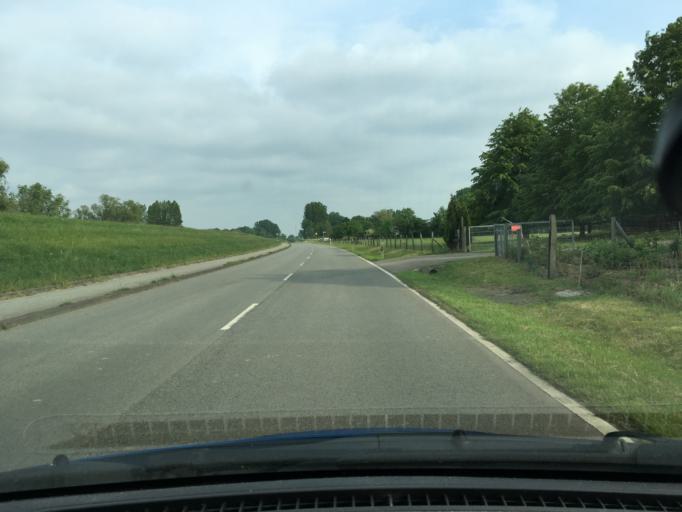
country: DE
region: Hamburg
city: Rothenburgsort
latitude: 53.4825
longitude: 10.0511
